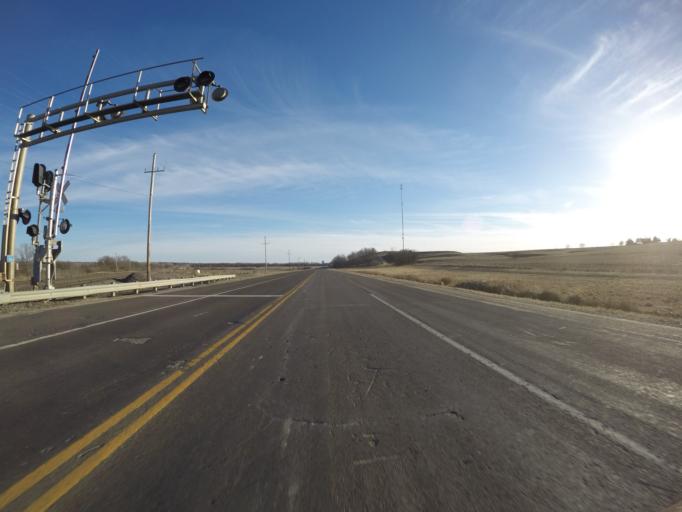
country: US
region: Kansas
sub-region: Marshall County
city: Marysville
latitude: 39.8747
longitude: -96.6665
